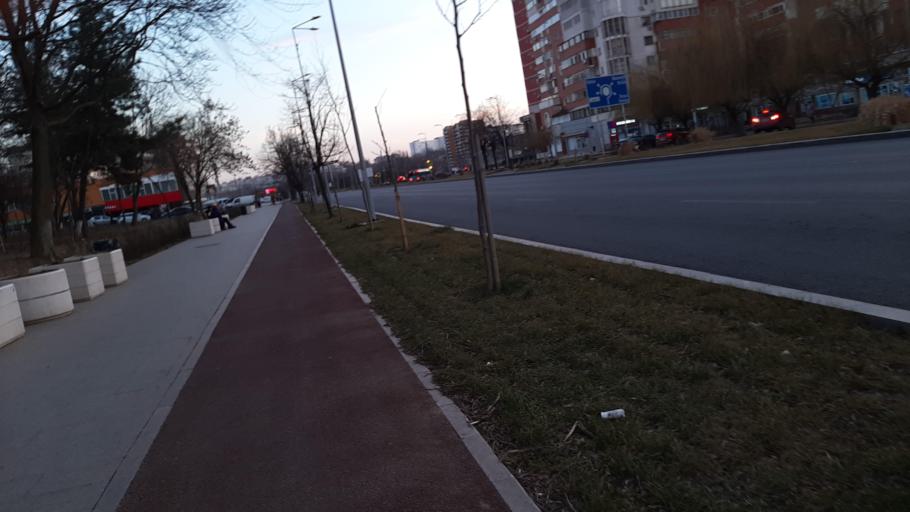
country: RO
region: Galati
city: Galati
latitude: 45.4295
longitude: 28.0250
